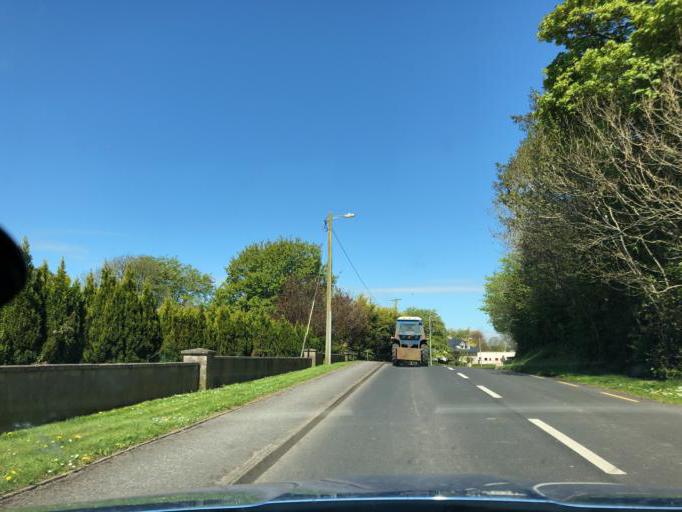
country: IE
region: Connaught
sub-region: County Galway
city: Portumna
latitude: 53.1460
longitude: -8.3707
